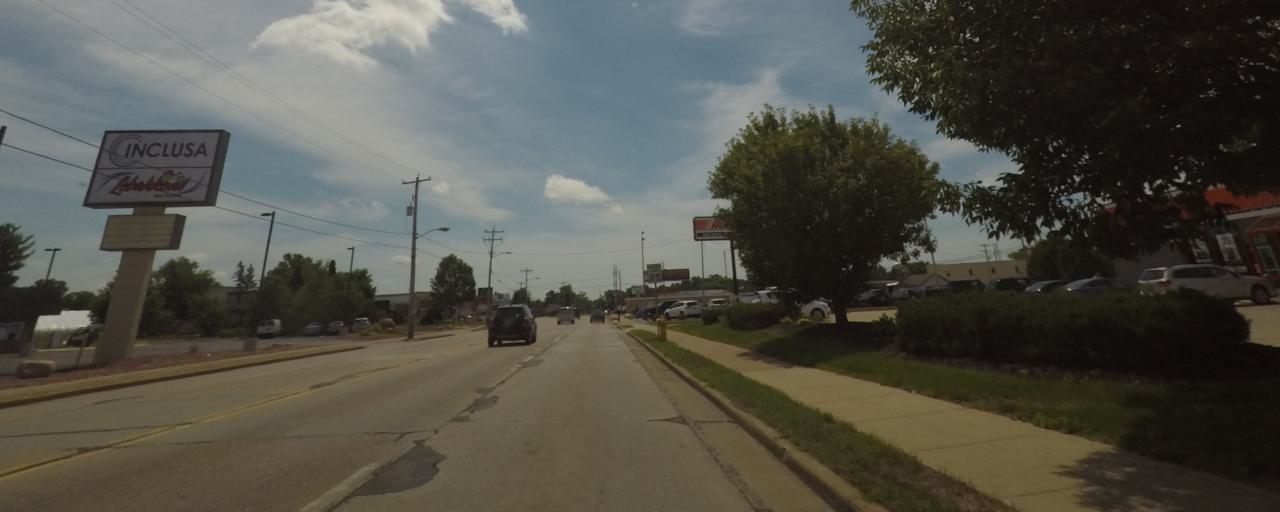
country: US
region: Wisconsin
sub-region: Portage County
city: Whiting
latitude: 44.5005
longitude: -89.5638
